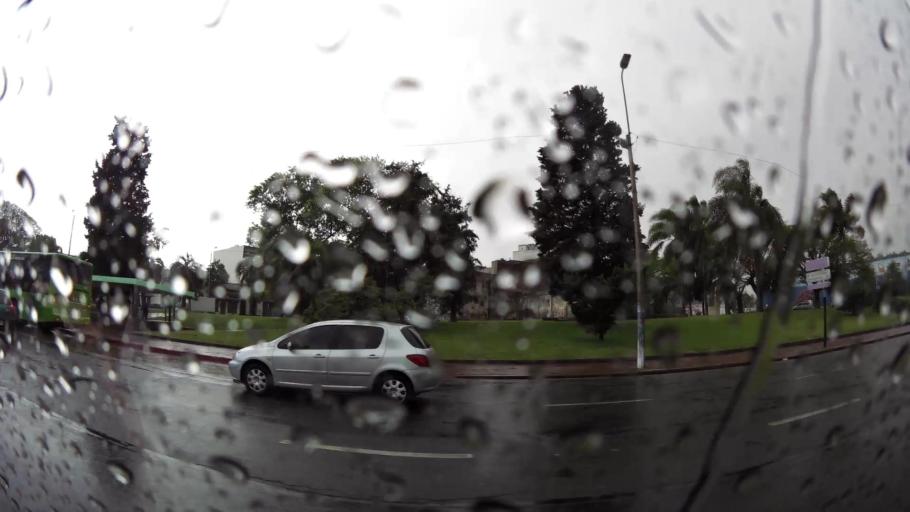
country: UY
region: Montevideo
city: Montevideo
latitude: -34.8921
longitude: -56.1864
